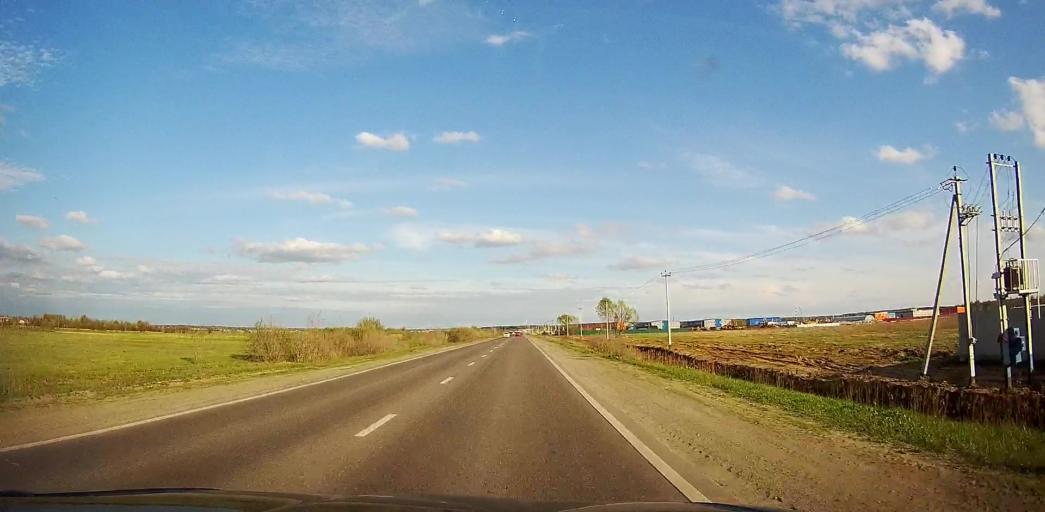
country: RU
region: Moskovskaya
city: Malyshevo
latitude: 55.4971
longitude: 38.3059
